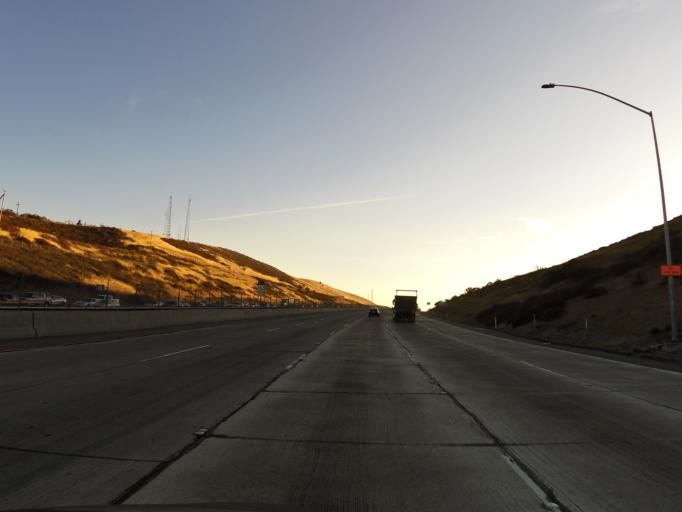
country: US
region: California
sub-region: Contra Costa County
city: Bay Point
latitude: 38.0169
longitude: -121.9906
